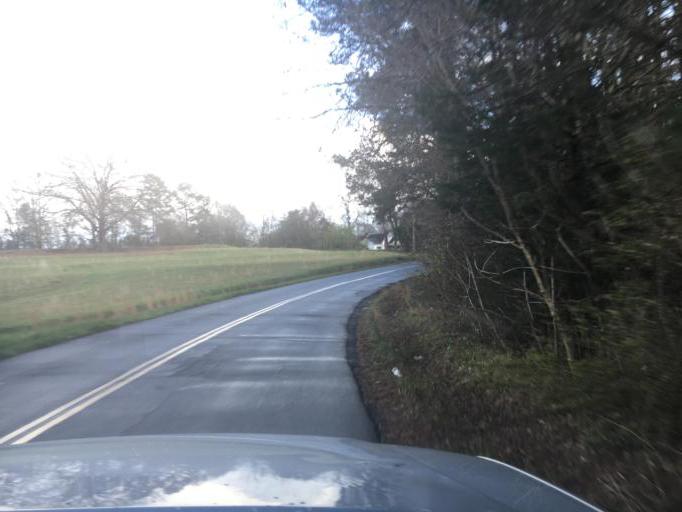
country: US
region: South Carolina
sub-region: Greenville County
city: Parker
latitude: 34.8619
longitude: -82.5026
